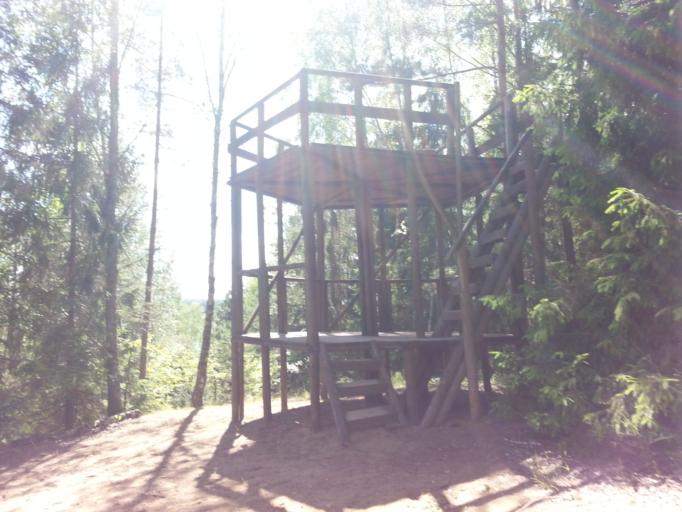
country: BY
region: Vitebsk
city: Lyntupy
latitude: 54.9655
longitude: 26.3847
